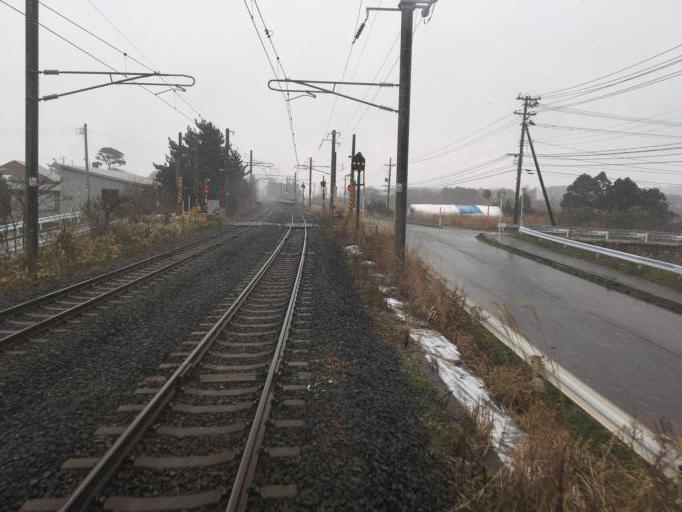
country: JP
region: Aomori
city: Aomori Shi
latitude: 40.9901
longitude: 140.6517
